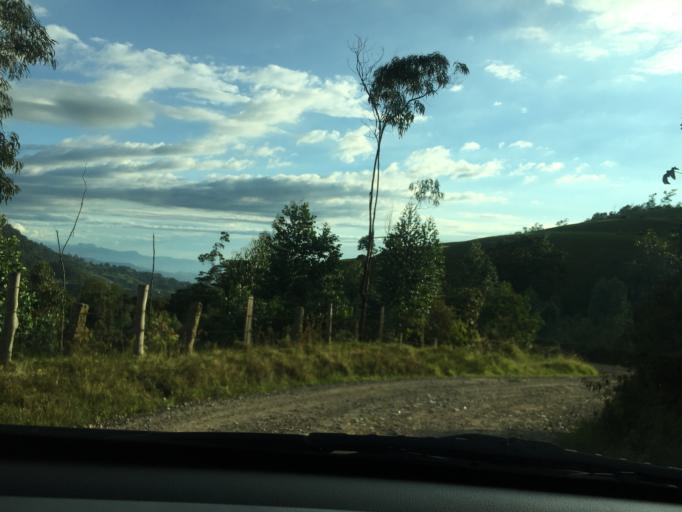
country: CO
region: Cundinamarca
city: Zipacon
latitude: 4.7312
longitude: -74.3902
